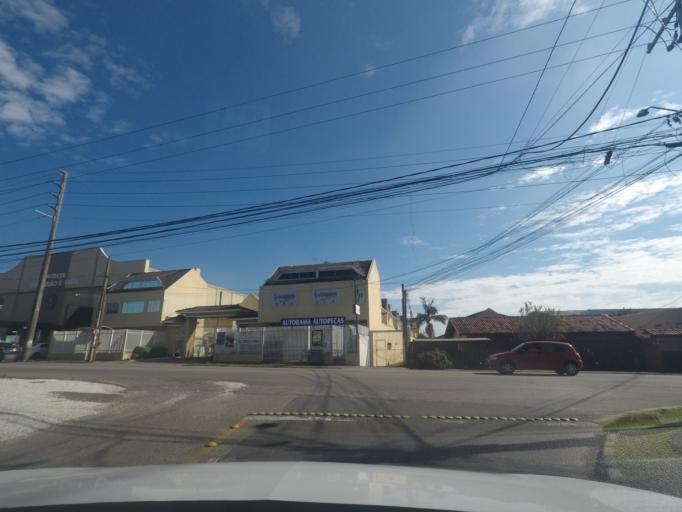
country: BR
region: Parana
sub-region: Curitiba
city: Curitiba
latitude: -25.4960
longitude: -49.2691
